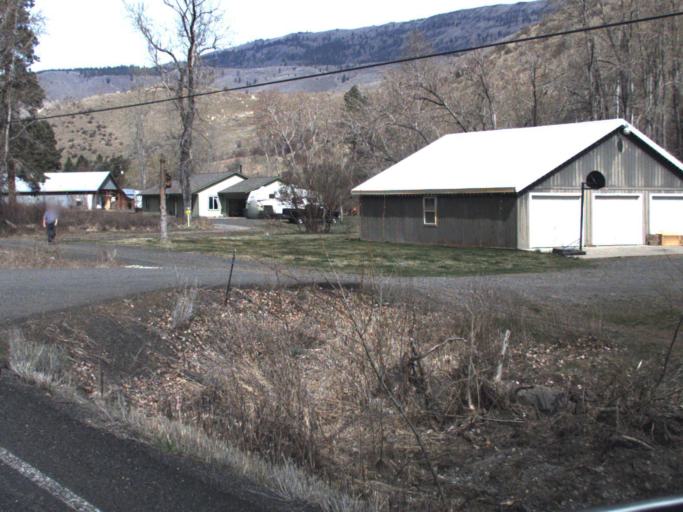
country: US
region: Washington
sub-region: Yakima County
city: Tieton
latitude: 46.7742
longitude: -120.8539
